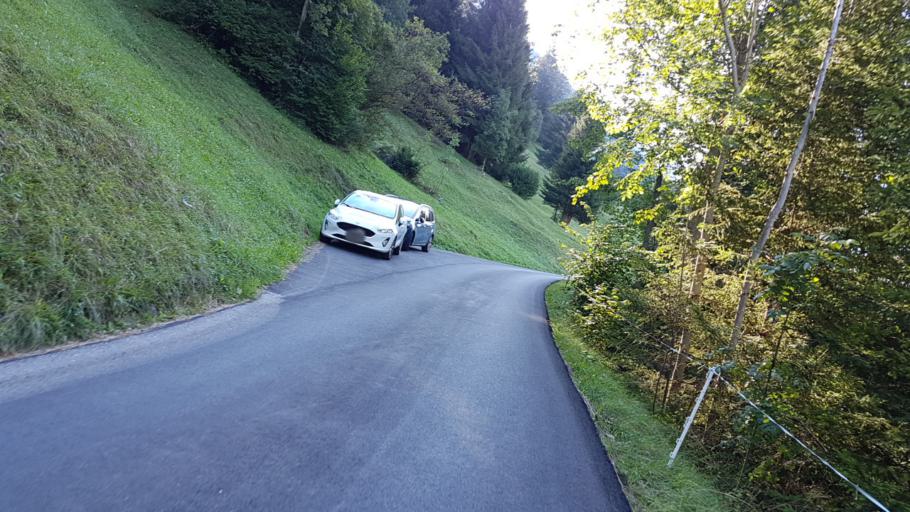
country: CH
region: Bern
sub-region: Frutigen-Niedersimmental District
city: Frutigen
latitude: 46.5578
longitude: 7.6699
